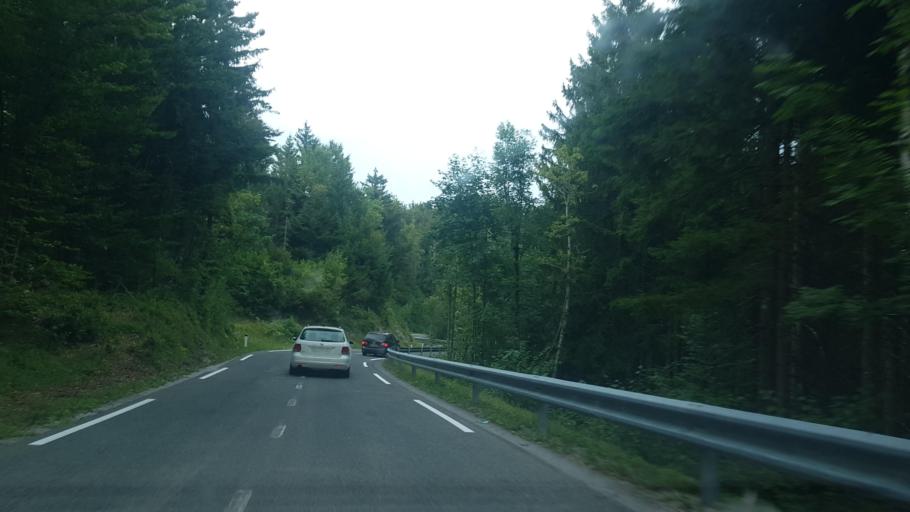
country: SI
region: Logatec
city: Logatec
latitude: 45.8911
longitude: 14.1630
